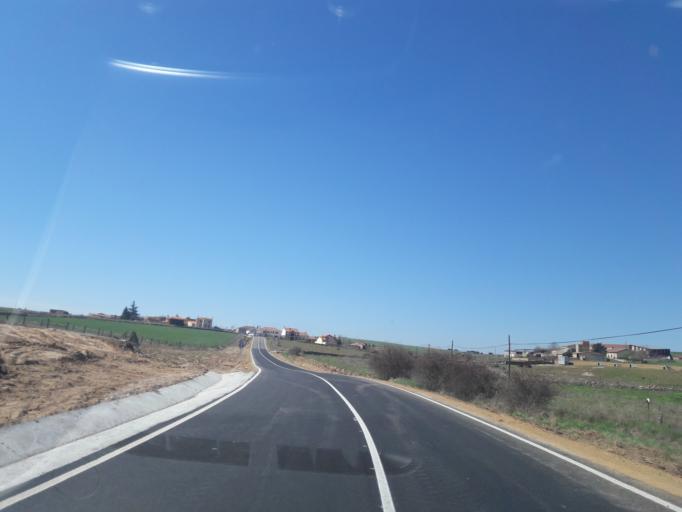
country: ES
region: Castille and Leon
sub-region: Provincia de Salamanca
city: Valdemierque
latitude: 40.8244
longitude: -5.5764
